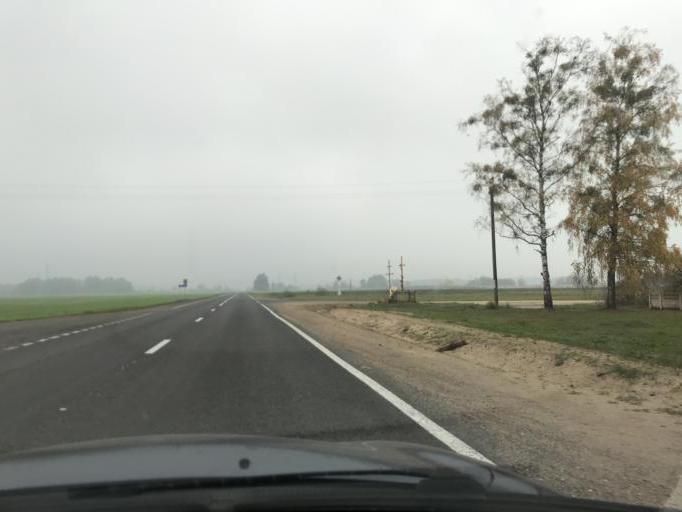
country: BY
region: Grodnenskaya
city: Hrodna
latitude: 53.8298
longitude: 23.8826
